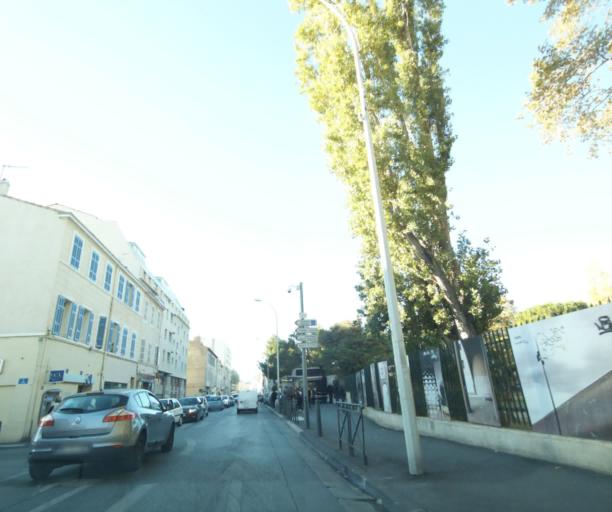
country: FR
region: Provence-Alpes-Cote d'Azur
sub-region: Departement des Bouches-du-Rhone
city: Marseille 10
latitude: 43.2796
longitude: 5.4108
